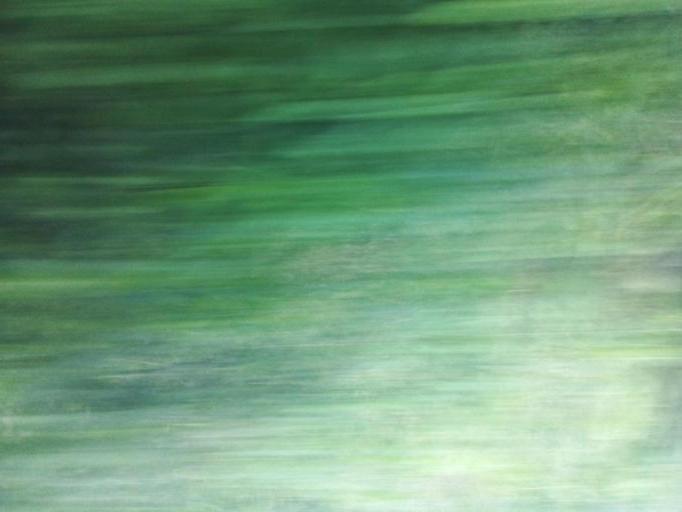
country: BR
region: Minas Gerais
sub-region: Belo Oriente
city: Belo Oriente
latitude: -19.2166
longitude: -42.2979
